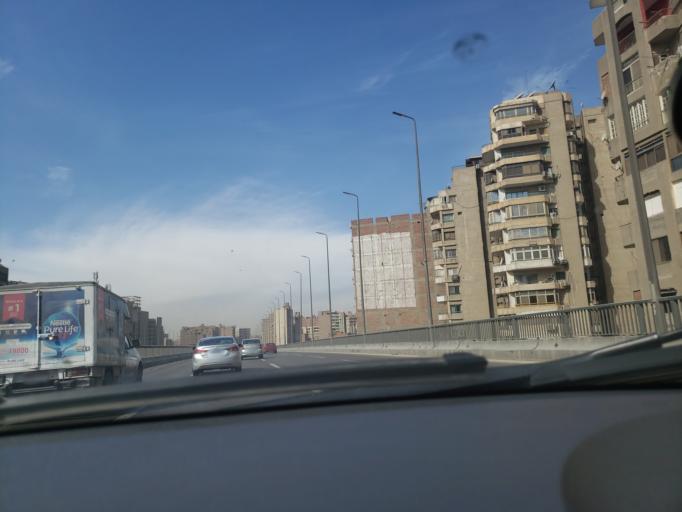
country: EG
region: Al Jizah
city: Al Jizah
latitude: 29.9827
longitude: 31.1560
